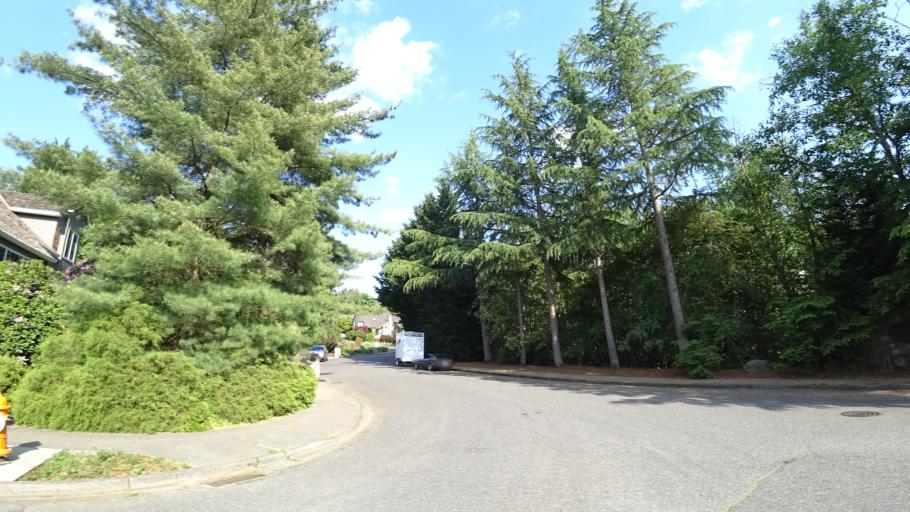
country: US
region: Oregon
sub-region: Washington County
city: Garden Home-Whitford
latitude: 45.4617
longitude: -122.7405
